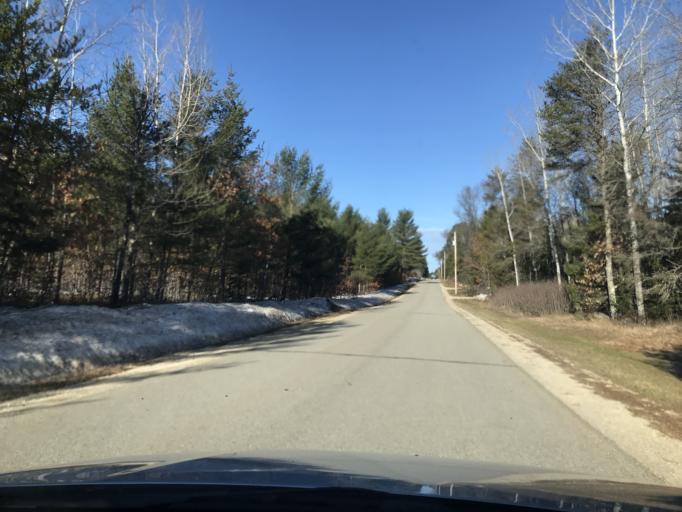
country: US
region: Wisconsin
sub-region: Marinette County
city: Niagara
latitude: 45.3985
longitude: -88.0912
